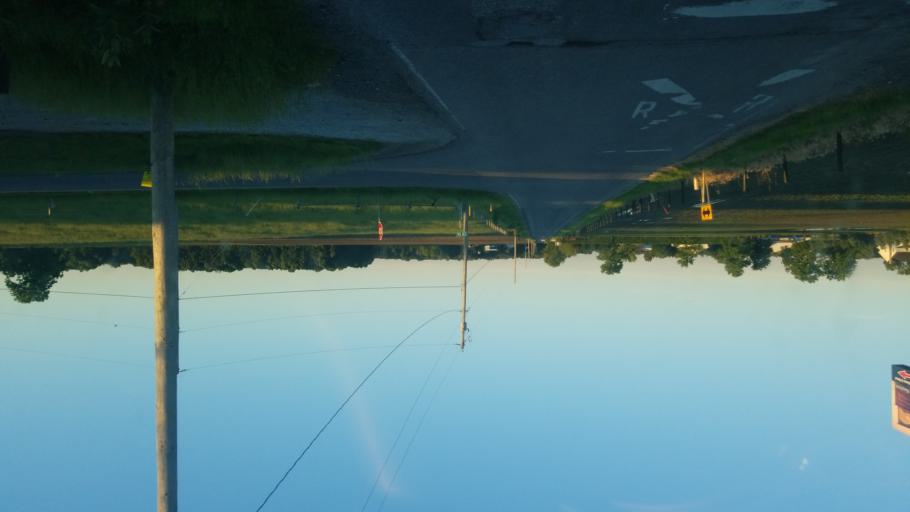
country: US
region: Indiana
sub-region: Elkhart County
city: Nappanee
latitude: 41.4430
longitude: -86.0304
